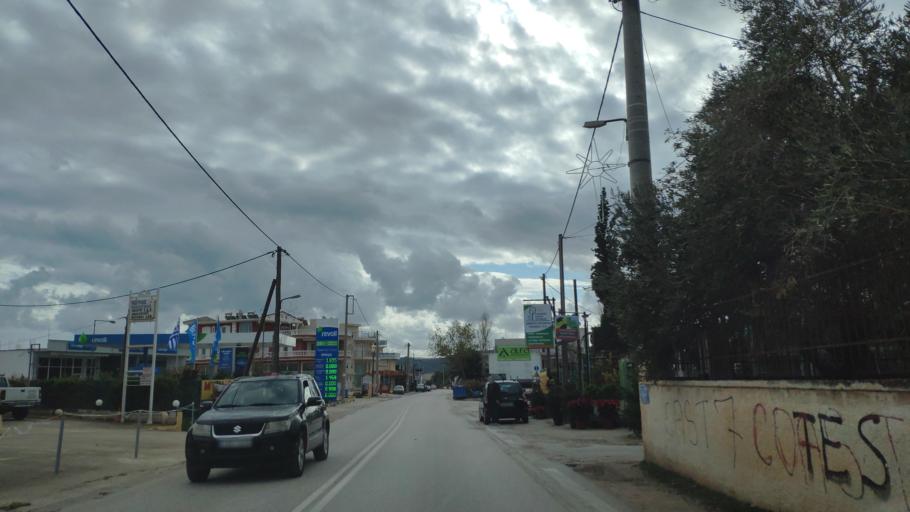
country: GR
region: Attica
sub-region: Nomarchia Anatolikis Attikis
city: Artemida
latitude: 37.9449
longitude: 24.0078
